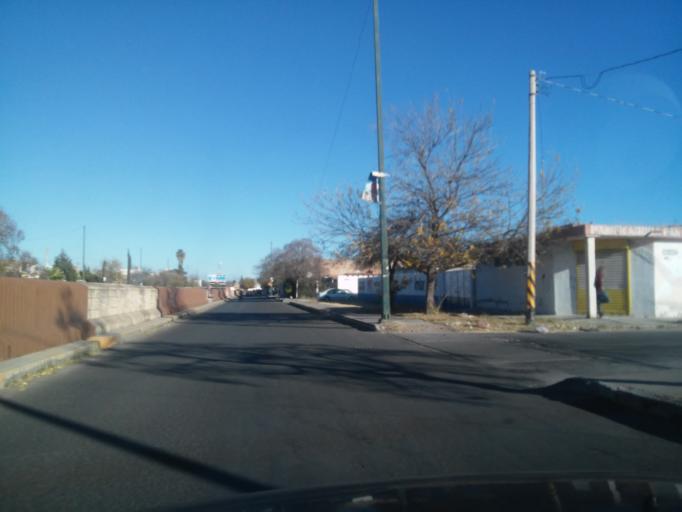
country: MX
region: Durango
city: Victoria de Durango
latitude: 24.0156
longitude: -104.6424
